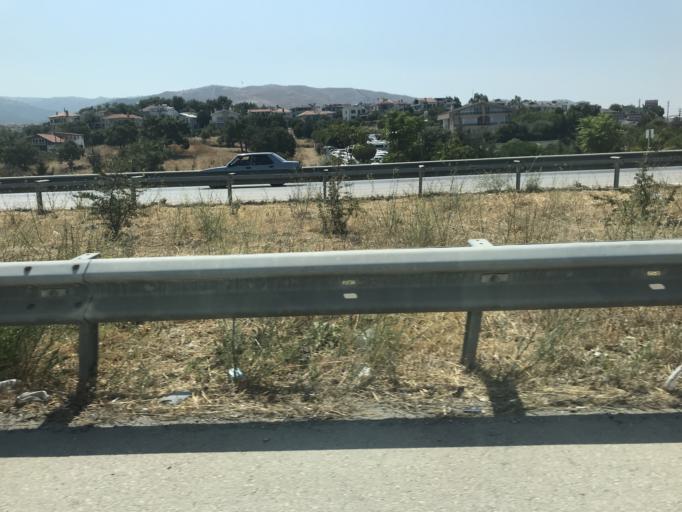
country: TR
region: Izmir
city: Urla
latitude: 38.3700
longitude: 26.8749
